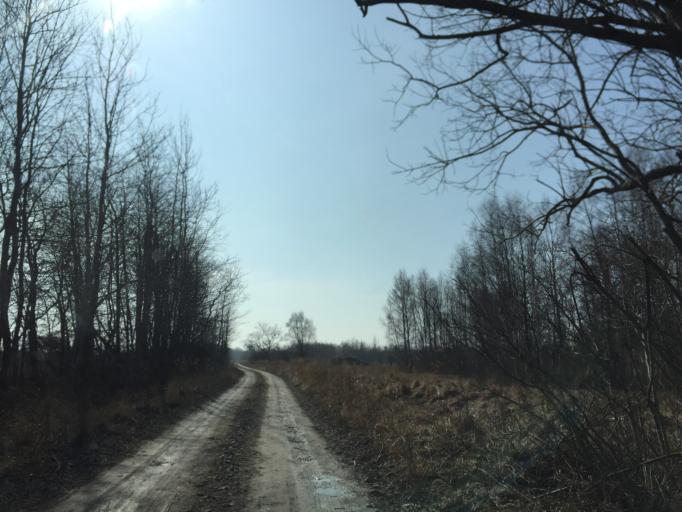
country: LV
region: Dundaga
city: Dundaga
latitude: 57.9308
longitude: 22.0636
